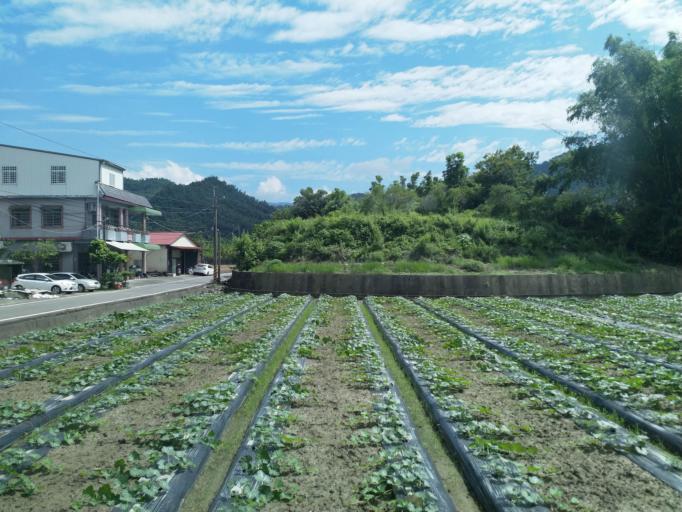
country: TW
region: Taiwan
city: Yujing
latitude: 22.9167
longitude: 120.5795
